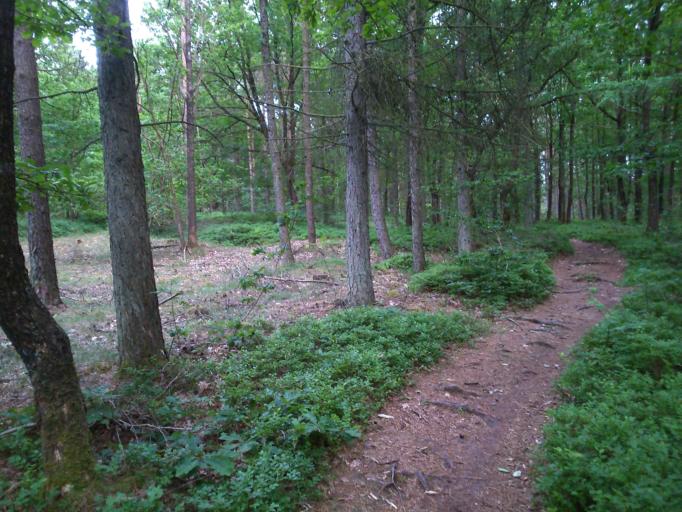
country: DK
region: Central Jutland
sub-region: Ringkobing-Skjern Kommune
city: Skjern
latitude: 55.9967
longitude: 8.4380
